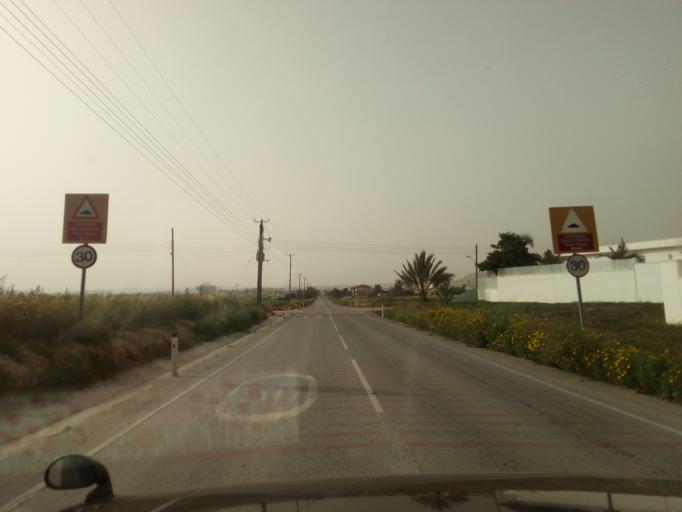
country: CY
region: Larnaka
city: Athienou
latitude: 35.0525
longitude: 33.5373
